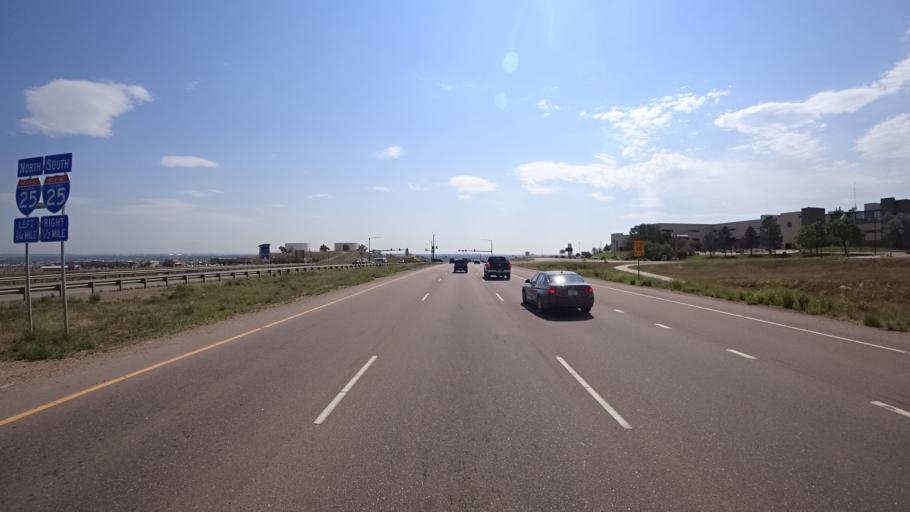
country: US
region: Colorado
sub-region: El Paso County
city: Stratmoor
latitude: 38.7657
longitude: -104.7883
